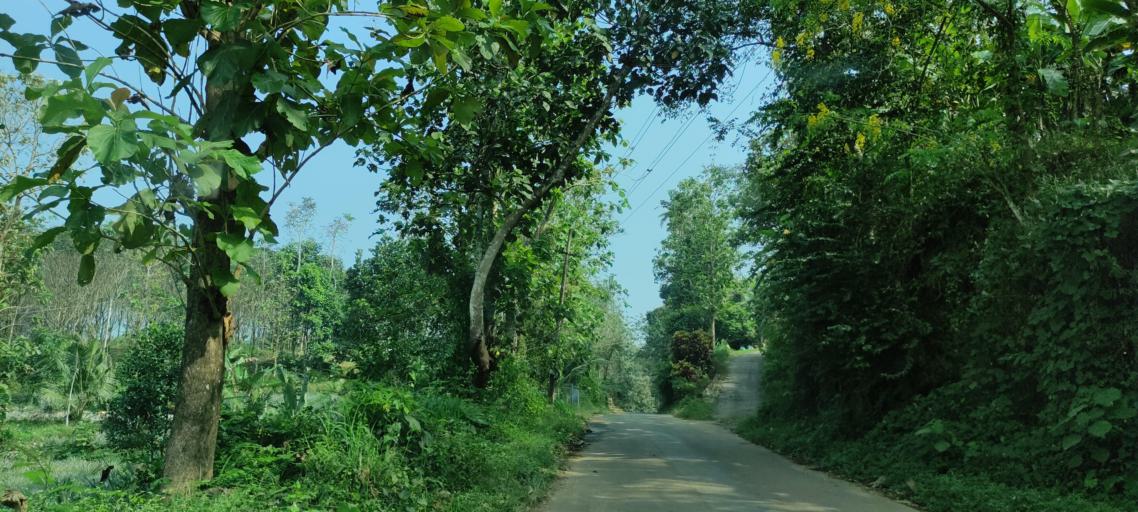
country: IN
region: Kerala
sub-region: Ernakulam
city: Piravam
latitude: 9.8235
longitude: 76.5071
